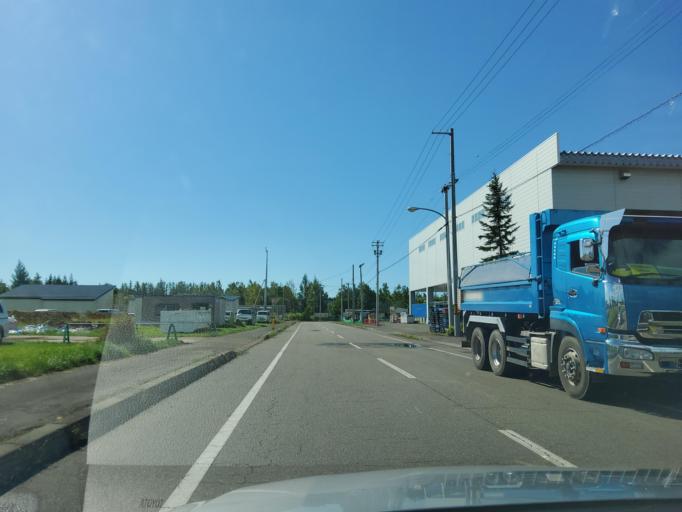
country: JP
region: Hokkaido
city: Otofuke
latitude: 42.9835
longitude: 143.1792
